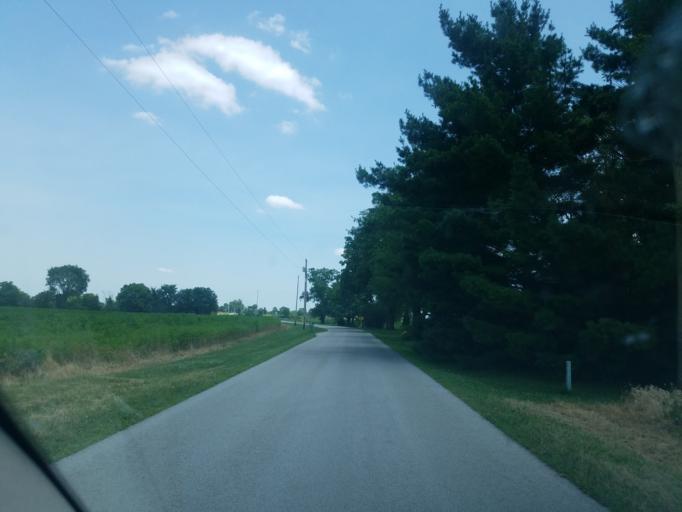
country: US
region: Ohio
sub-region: Wyandot County
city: Carey
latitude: 40.9465
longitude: -83.5094
